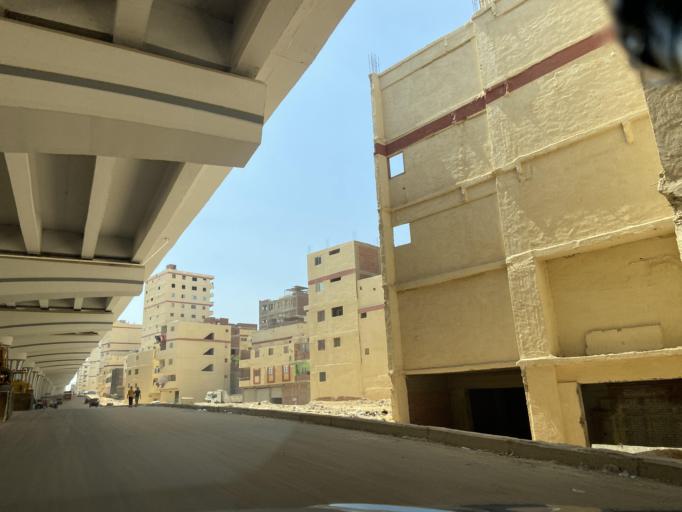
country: EG
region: Muhafazat al Qahirah
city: Cairo
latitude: 30.0677
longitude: 31.3847
